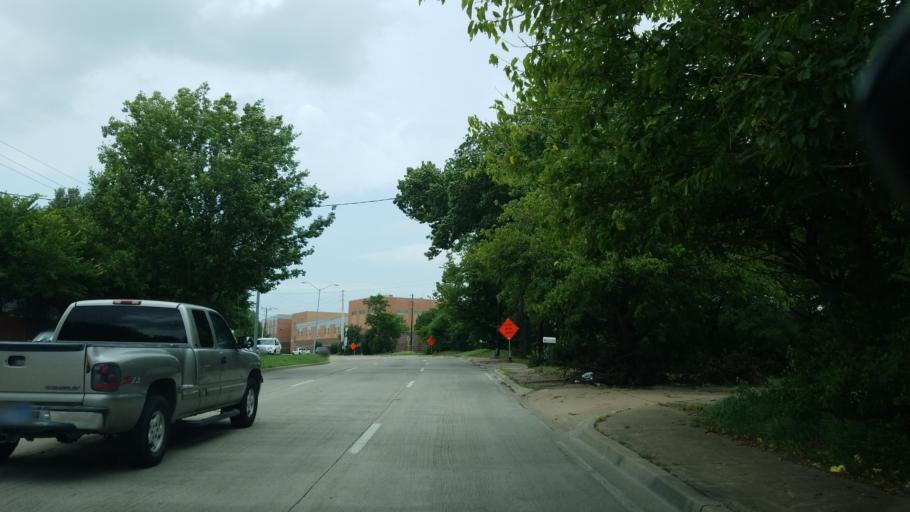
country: US
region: Texas
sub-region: Dallas County
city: Farmers Branch
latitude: 32.8780
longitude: -96.8645
